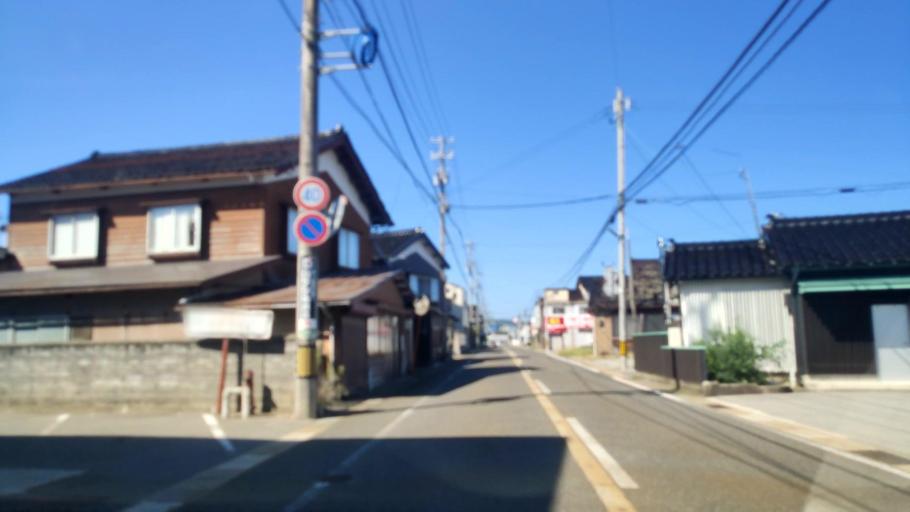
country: JP
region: Ishikawa
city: Nanao
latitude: 37.4412
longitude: 137.2649
